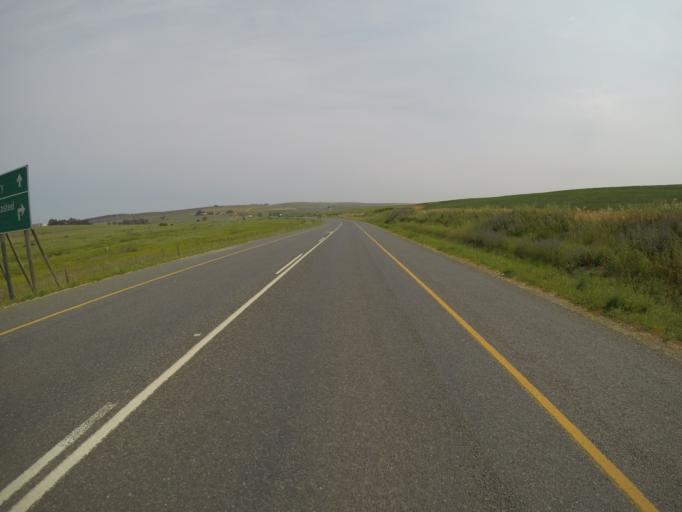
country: ZA
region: Western Cape
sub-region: West Coast District Municipality
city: Malmesbury
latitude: -33.4481
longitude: 18.7683
